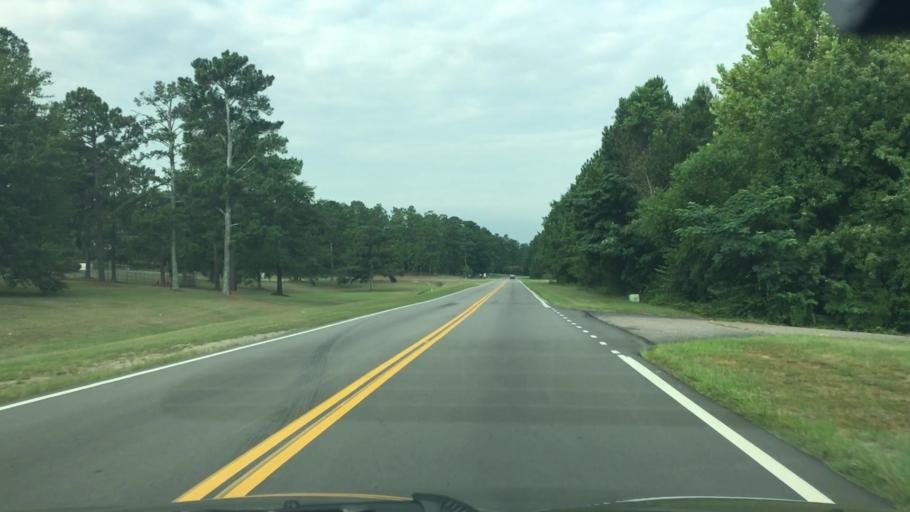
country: US
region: South Carolina
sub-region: Aiken County
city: Aiken
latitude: 33.6562
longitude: -81.6853
